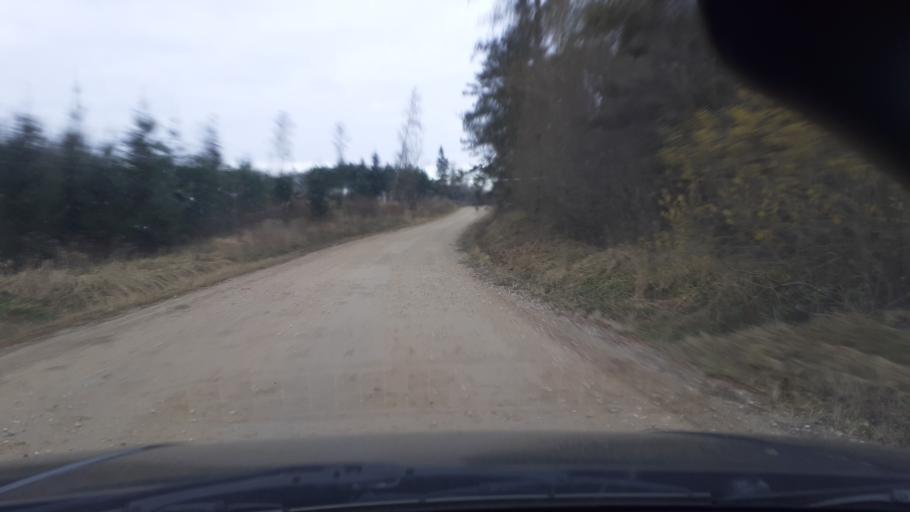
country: LV
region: Alsunga
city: Alsunga
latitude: 56.9628
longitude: 21.6531
